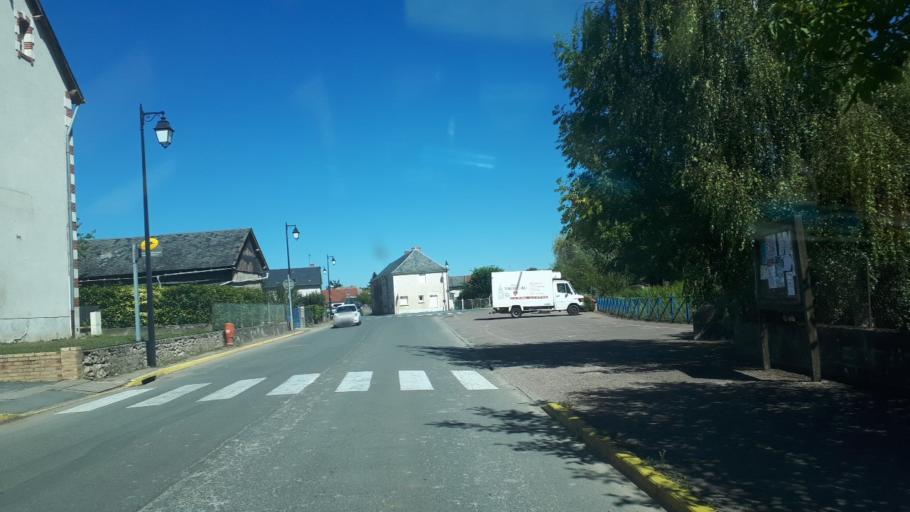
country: FR
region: Centre
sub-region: Departement du Cher
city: Sainte-Solange
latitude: 47.1364
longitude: 2.5511
